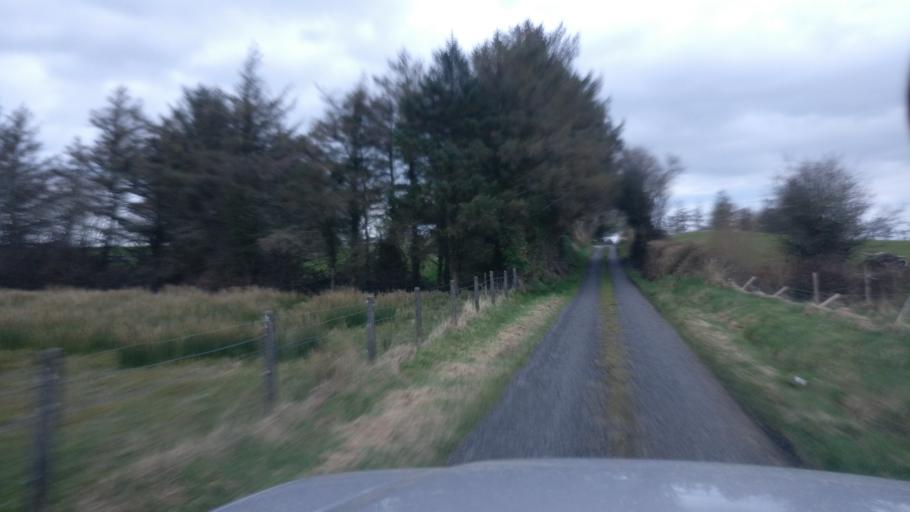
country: IE
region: Connaught
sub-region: County Galway
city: Loughrea
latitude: 53.2597
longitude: -8.4947
